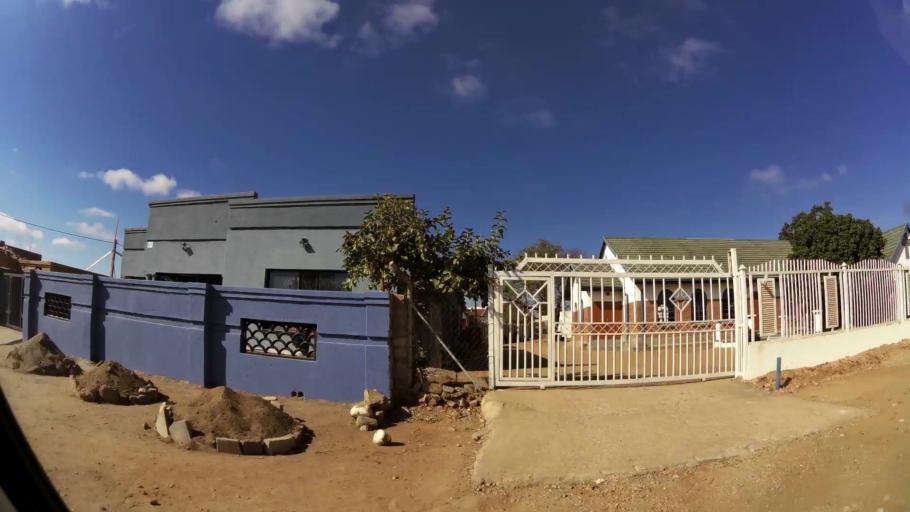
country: ZA
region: Limpopo
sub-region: Capricorn District Municipality
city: Polokwane
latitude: -23.8589
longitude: 29.3647
